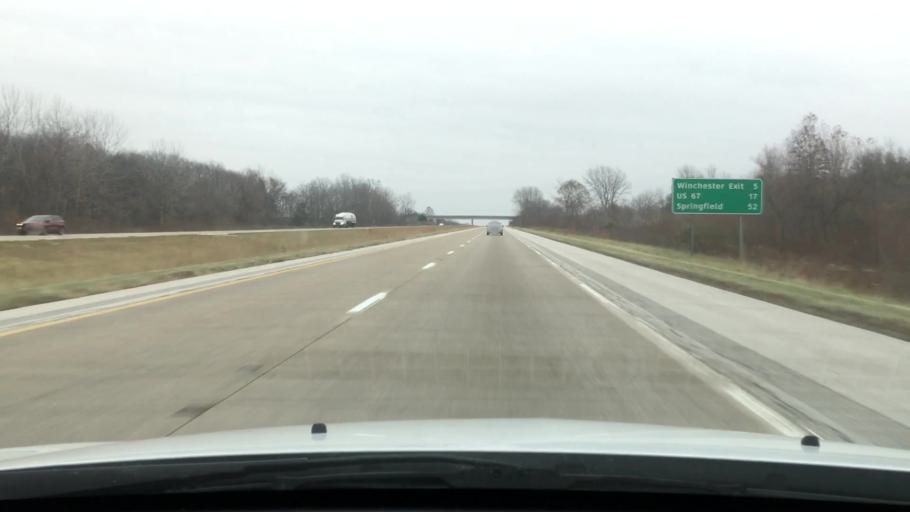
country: US
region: Illinois
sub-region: Scott County
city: Winchester
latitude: 39.6846
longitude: -90.5537
